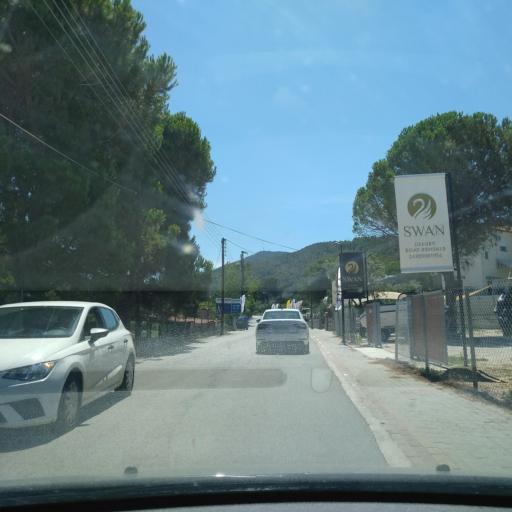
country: GR
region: Central Macedonia
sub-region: Nomos Chalkidikis
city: Neos Marmaras
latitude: 40.1890
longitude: 23.7781
